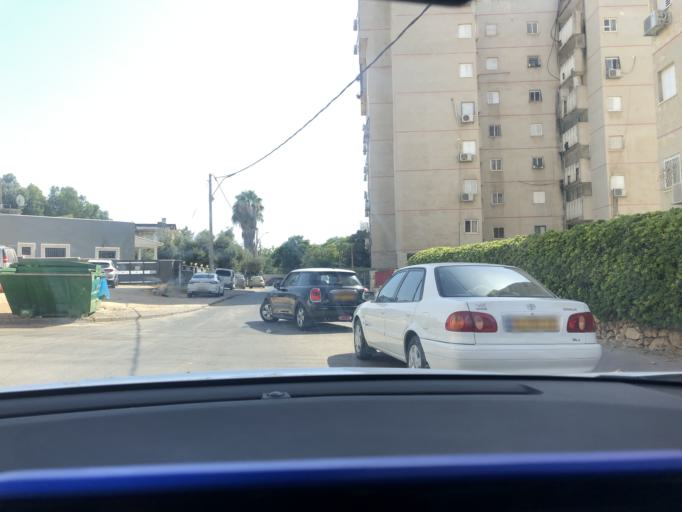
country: IL
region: Central District
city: Lod
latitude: 31.9497
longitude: 34.8921
